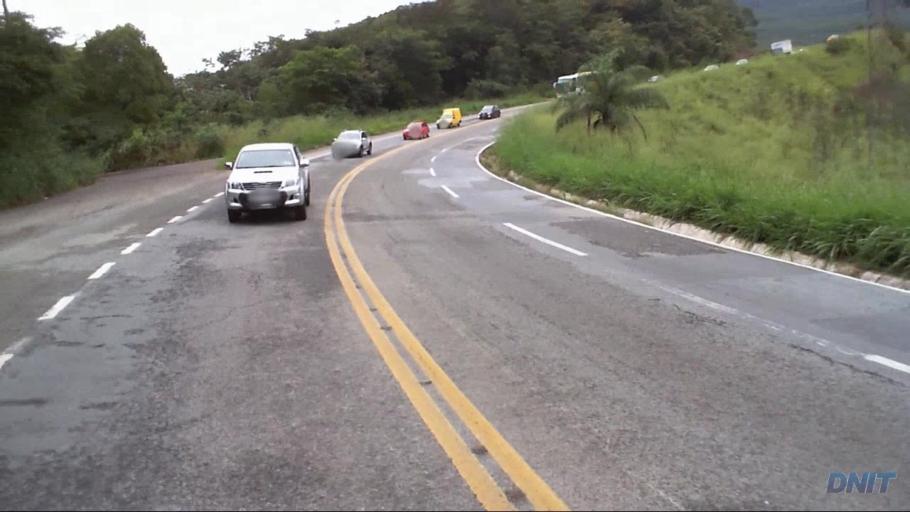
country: BR
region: Minas Gerais
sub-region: Joao Monlevade
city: Joao Monlevade
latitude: -19.8392
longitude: -43.3221
